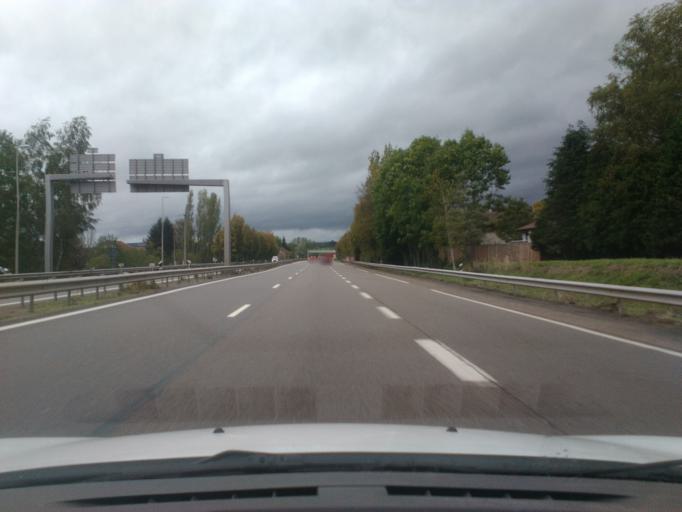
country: FR
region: Lorraine
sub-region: Departement des Vosges
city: Saint-Michel-sur-Meurthe
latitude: 48.3118
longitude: 6.9198
